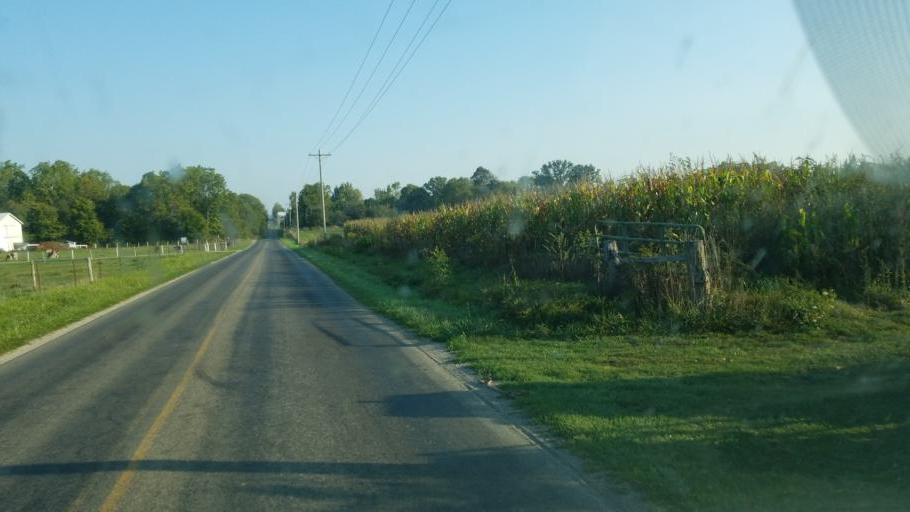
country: US
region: Indiana
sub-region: LaGrange County
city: Lagrange
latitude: 41.5888
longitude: -85.4241
